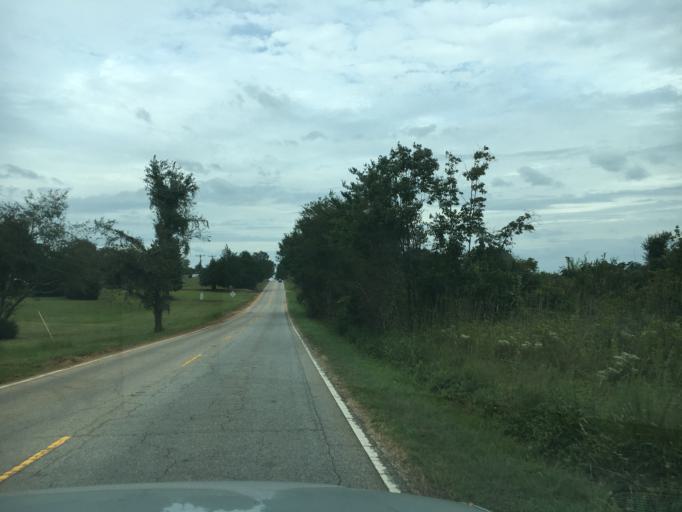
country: US
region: South Carolina
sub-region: Spartanburg County
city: Duncan
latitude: 34.9368
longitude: -82.1777
